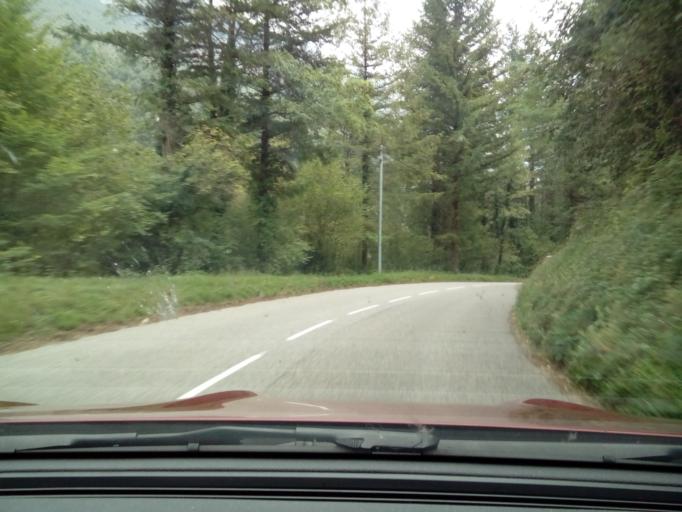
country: FR
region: Rhone-Alpes
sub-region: Departement de l'Isere
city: Pont-en-Royans
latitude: 45.0421
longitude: 5.3731
